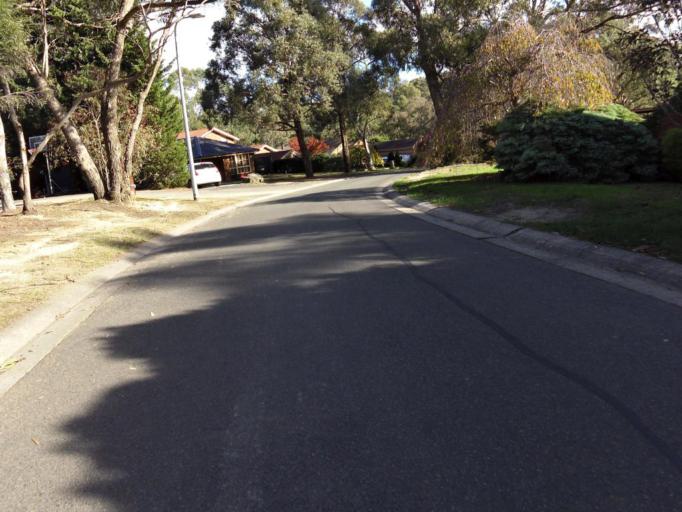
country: AU
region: Victoria
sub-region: Maroondah
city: Croydon Hills
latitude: -37.7720
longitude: 145.2640
